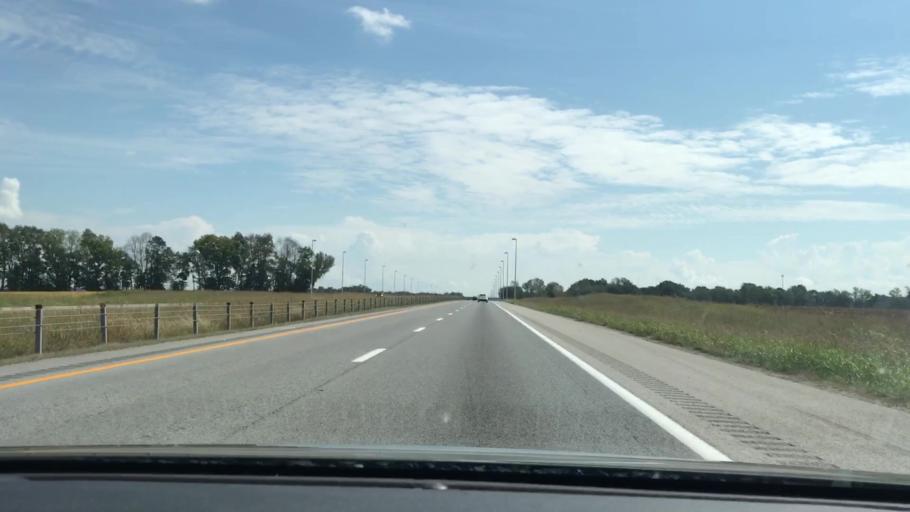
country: US
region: Kentucky
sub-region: Christian County
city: Fort Campbell North
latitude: 36.7488
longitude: -87.5195
